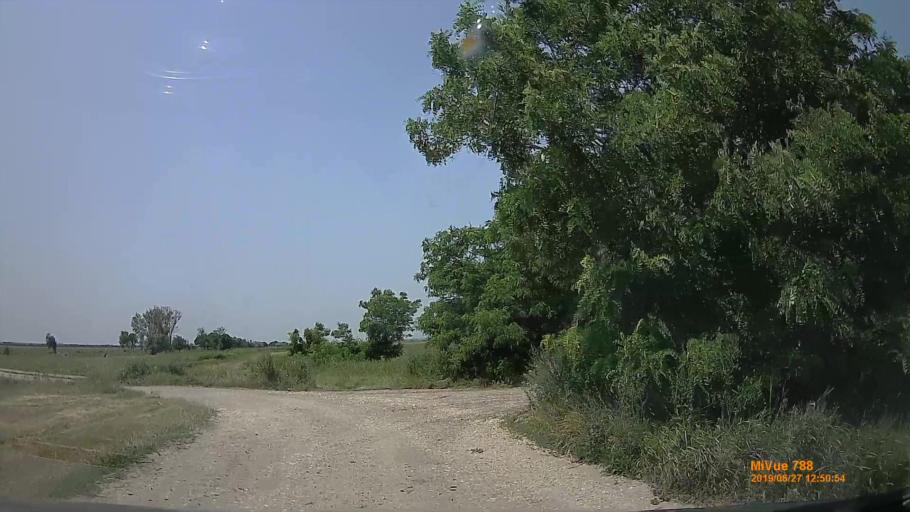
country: HU
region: Pest
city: Tortel
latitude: 47.1916
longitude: 19.8889
